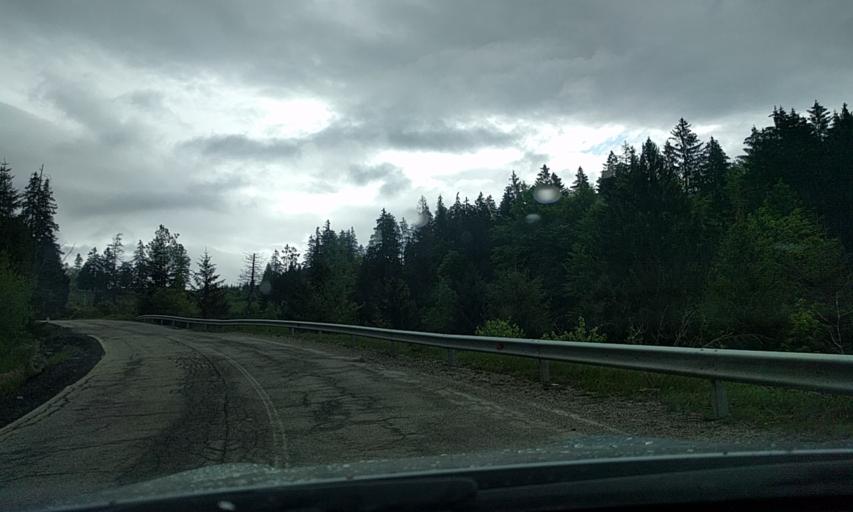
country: RO
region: Prahova
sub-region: Oras Sinaia
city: Sinaia
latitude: 45.3057
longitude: 25.5190
